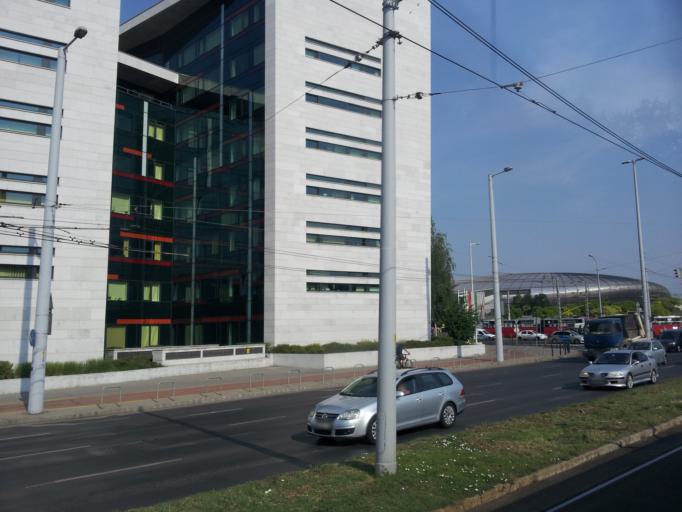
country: HU
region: Budapest
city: Budapest XIV. keruelet
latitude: 47.4993
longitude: 19.1083
